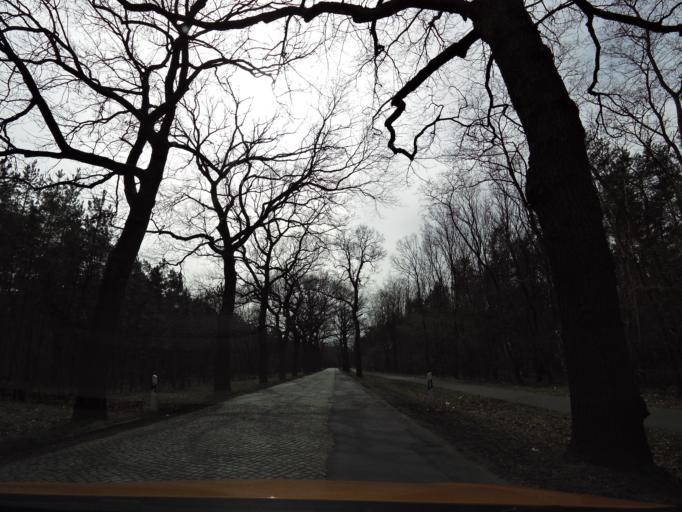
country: DE
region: Brandenburg
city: Rangsdorf
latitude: 52.3190
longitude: 13.3883
